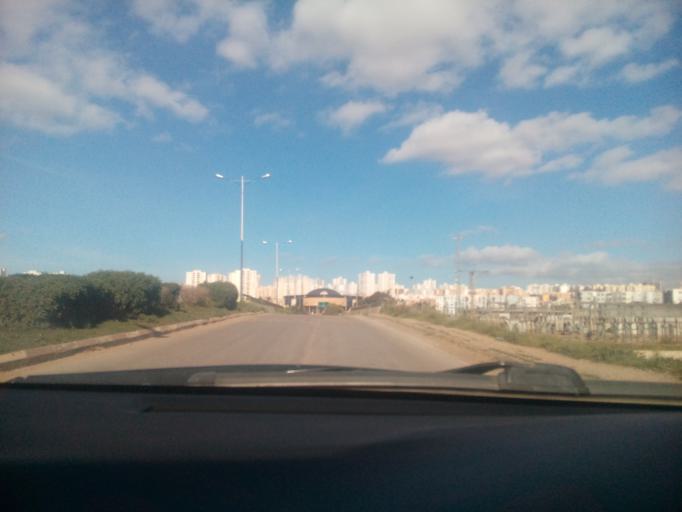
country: DZ
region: Oran
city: Bir el Djir
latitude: 35.6920
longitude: -0.5754
